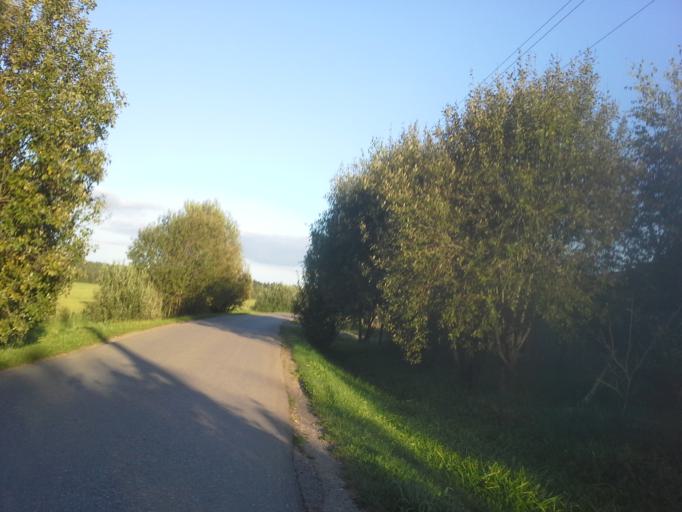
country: RU
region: Moskovskaya
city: Kievskij
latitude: 55.4686
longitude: 36.8784
